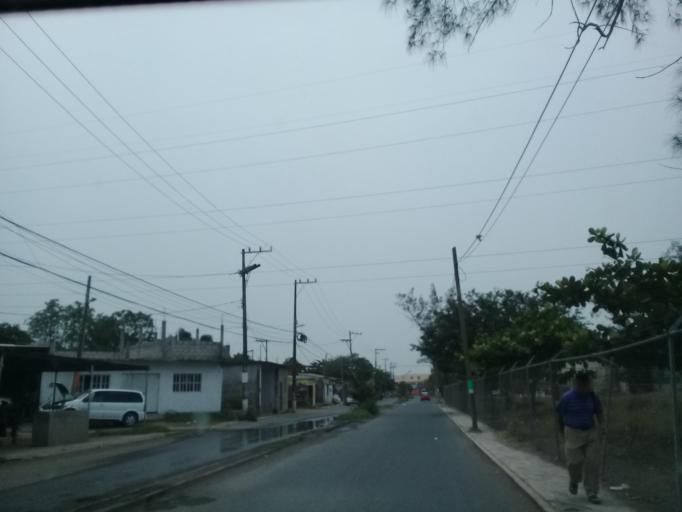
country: MX
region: Veracruz
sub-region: Veracruz
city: Las Amapolas
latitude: 19.1598
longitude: -96.2084
